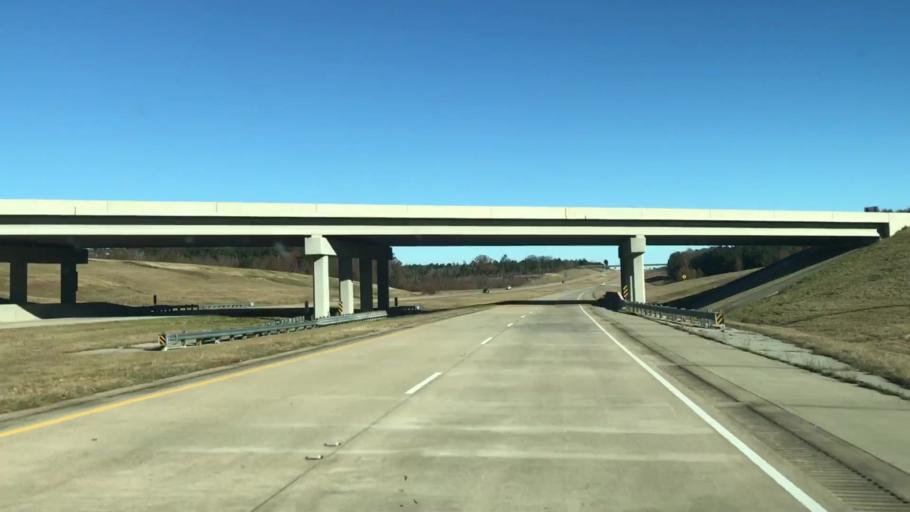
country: US
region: Louisiana
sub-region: Caddo Parish
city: Vivian
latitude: 32.9968
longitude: -93.9092
